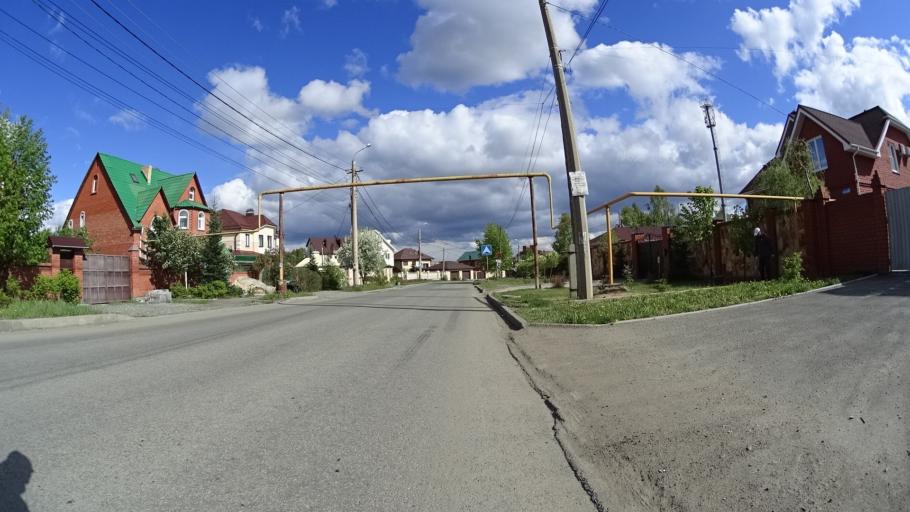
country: RU
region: Chelyabinsk
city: Sargazy
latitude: 55.1549
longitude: 61.2534
